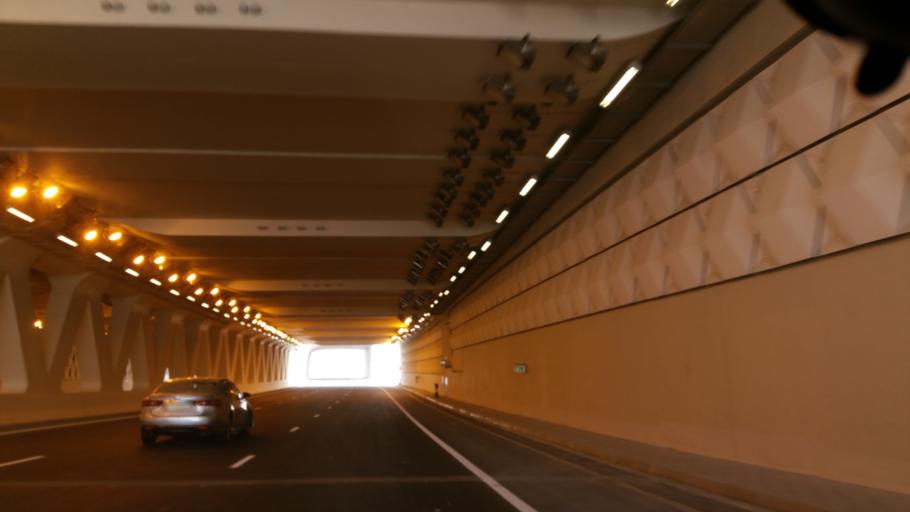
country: QA
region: Baladiyat Umm Salal
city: Umm Salal Muhammad
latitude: 25.4061
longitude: 51.5127
